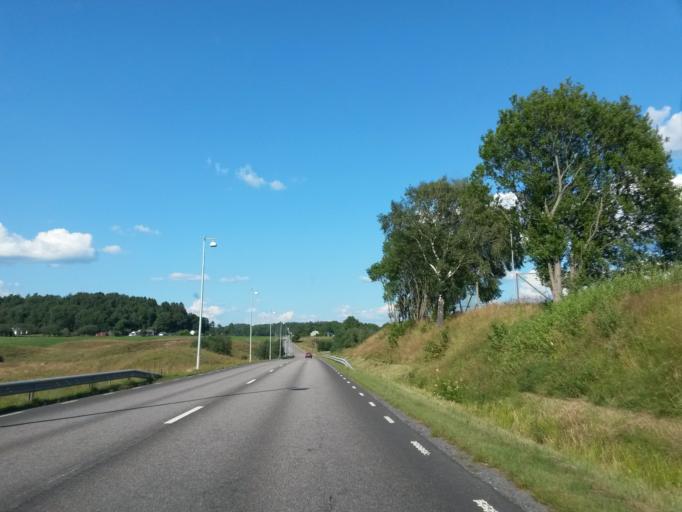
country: SE
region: Vaestra Goetaland
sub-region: Partille Kommun
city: Partille
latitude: 57.8062
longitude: 12.1669
